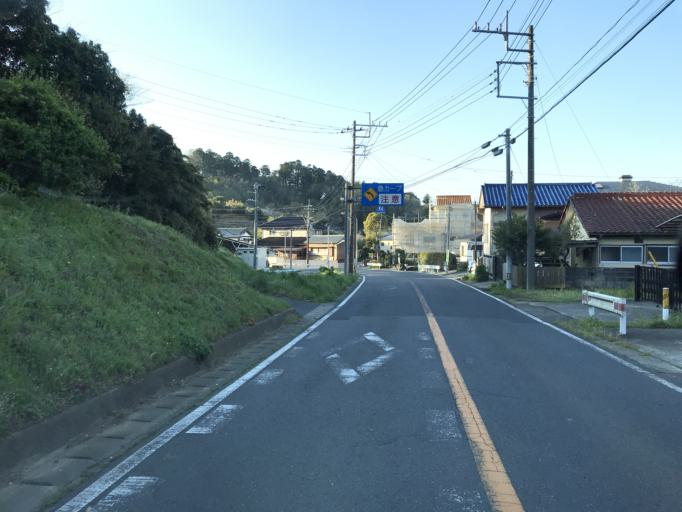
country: JP
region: Chiba
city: Yokaichiba
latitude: 35.7335
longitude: 140.5570
